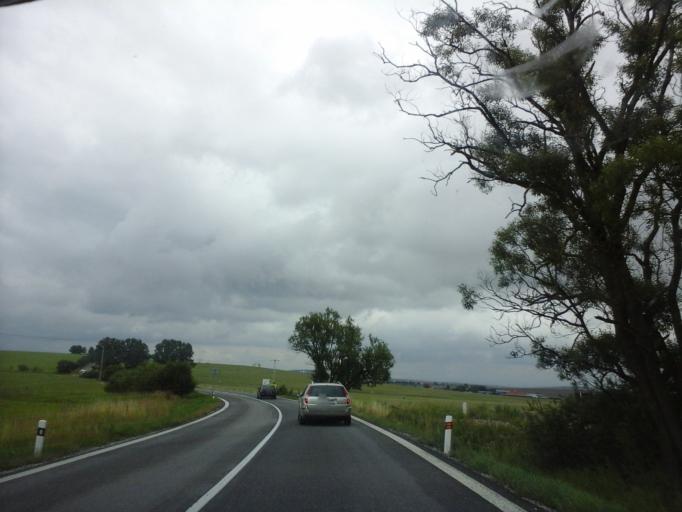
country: SK
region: Presovsky
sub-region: Okres Poprad
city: Poprad
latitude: 49.0275
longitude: 20.2836
